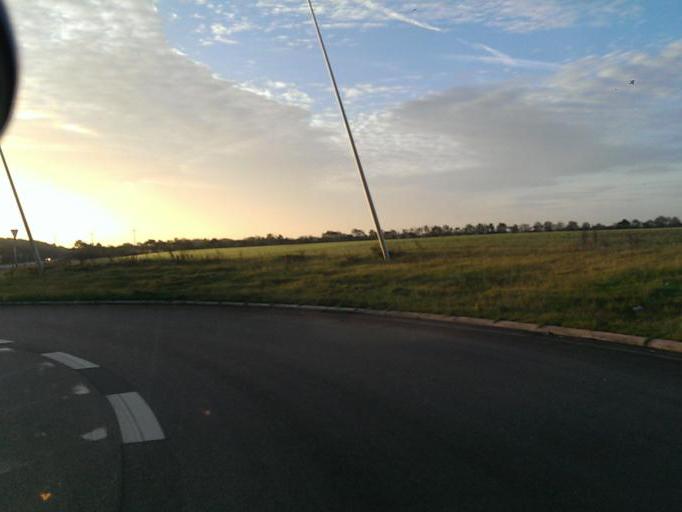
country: DK
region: South Denmark
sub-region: Esbjerg Kommune
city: Bramming
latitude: 55.4706
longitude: 8.6639
